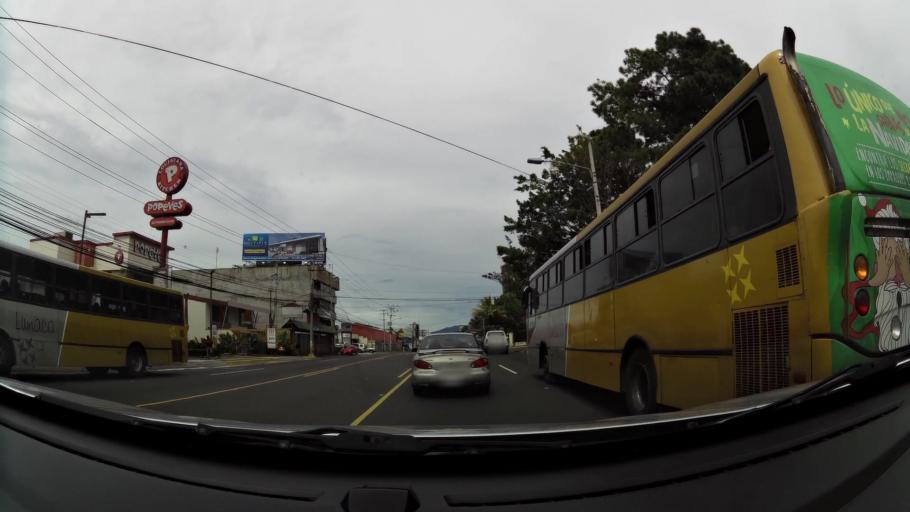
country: CR
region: San Jose
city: San Pedro
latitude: 9.9243
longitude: -84.0388
